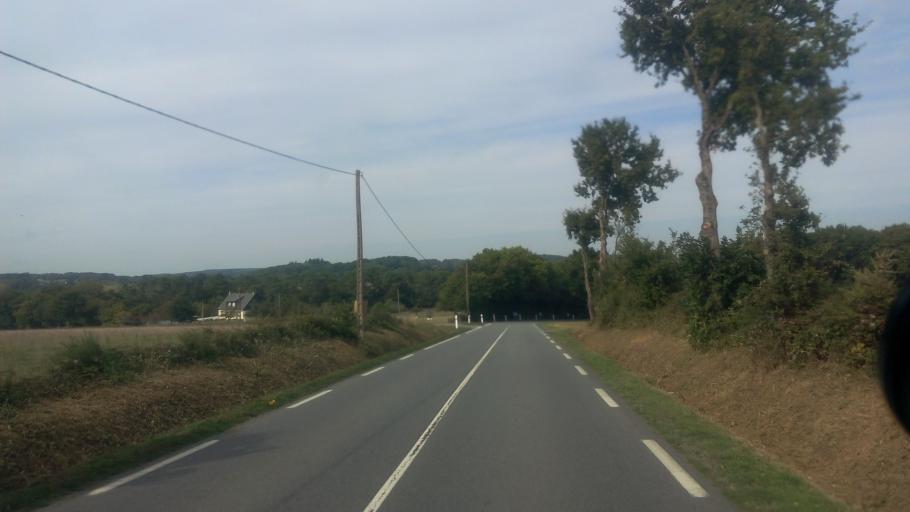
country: FR
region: Brittany
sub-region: Departement d'Ille-et-Vilaine
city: Bains-sur-Oust
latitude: 47.7258
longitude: -2.1044
